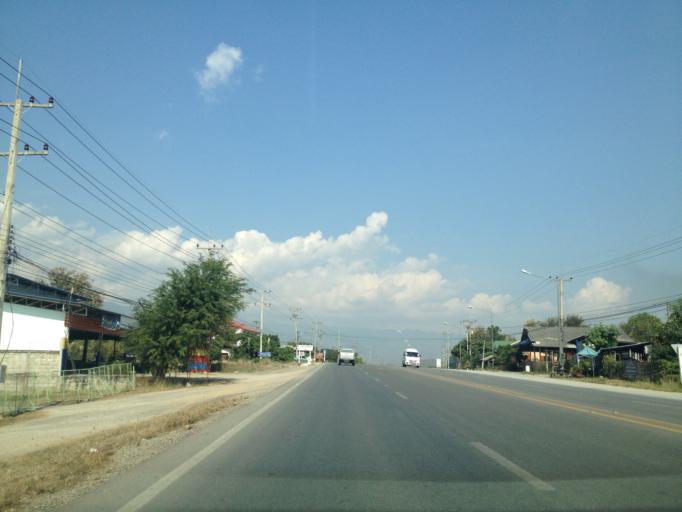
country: TH
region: Chiang Mai
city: Hot
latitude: 18.2124
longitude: 98.6155
